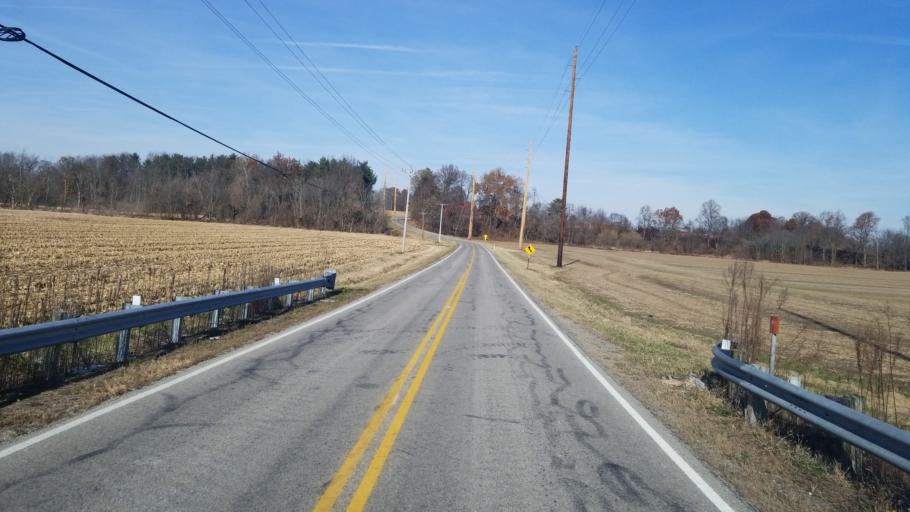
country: US
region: Ohio
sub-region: Huron County
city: Willard
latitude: 41.1253
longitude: -82.6862
